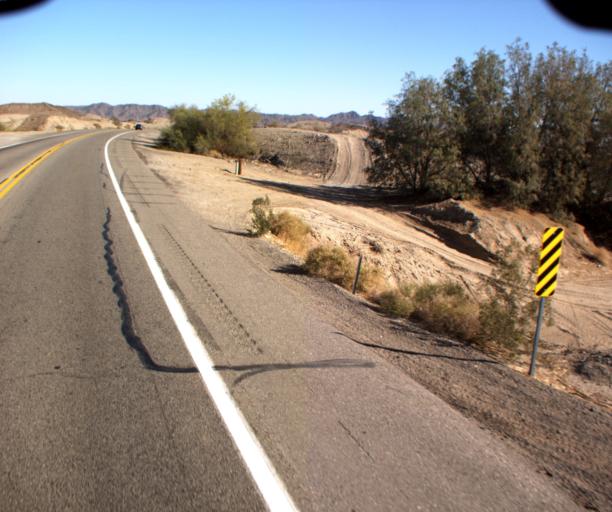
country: US
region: Arizona
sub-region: Yuma County
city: Fortuna Foothills
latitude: 32.7392
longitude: -114.4255
